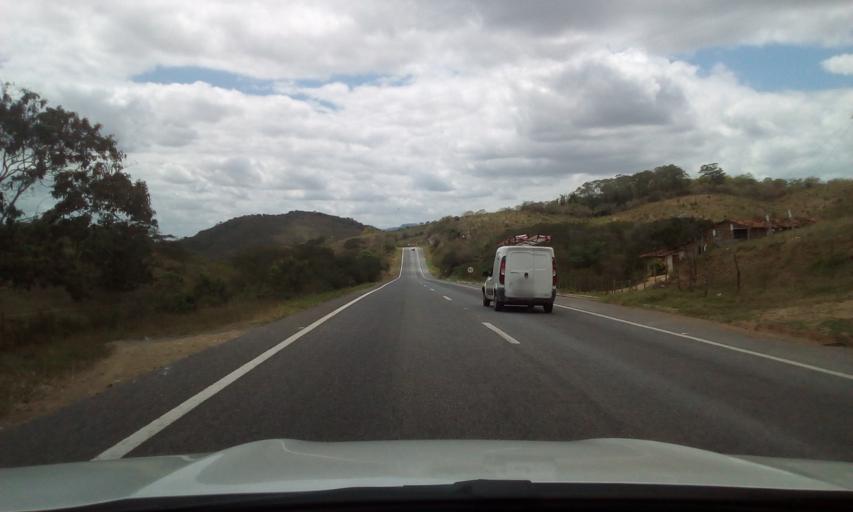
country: BR
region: Paraiba
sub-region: Inga
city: Inga
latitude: -7.2608
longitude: -35.6946
